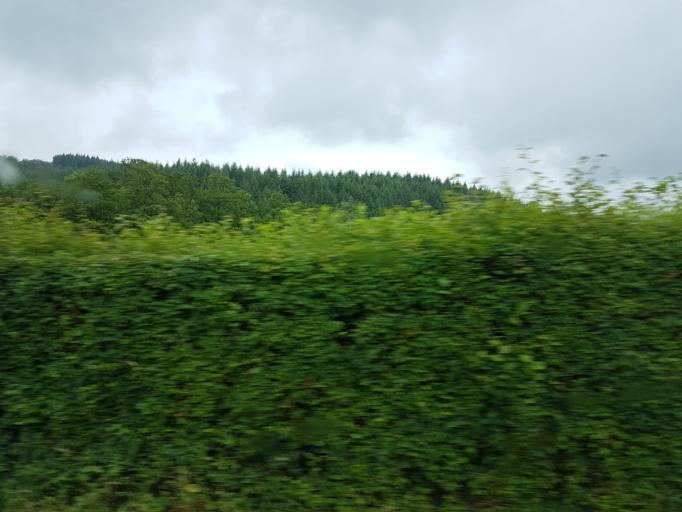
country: FR
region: Bourgogne
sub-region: Departement de la Nievre
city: Lormes
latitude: 47.1752
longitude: 3.8342
